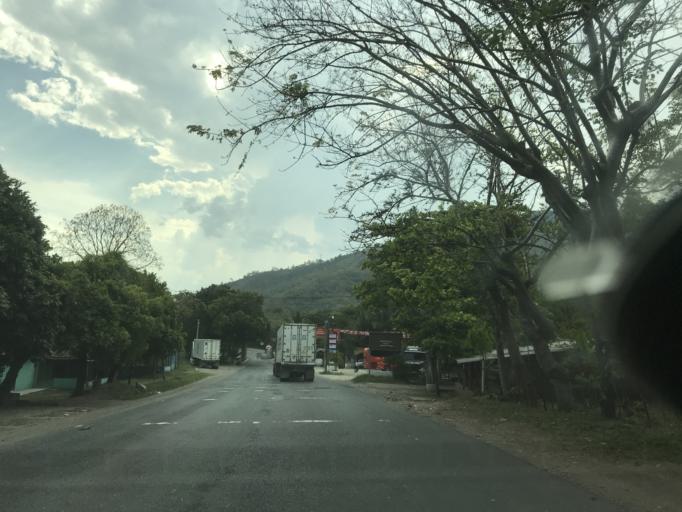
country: GT
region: Zacapa
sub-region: Municipio de Zacapa
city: Gualan
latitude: 15.2076
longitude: -89.2485
